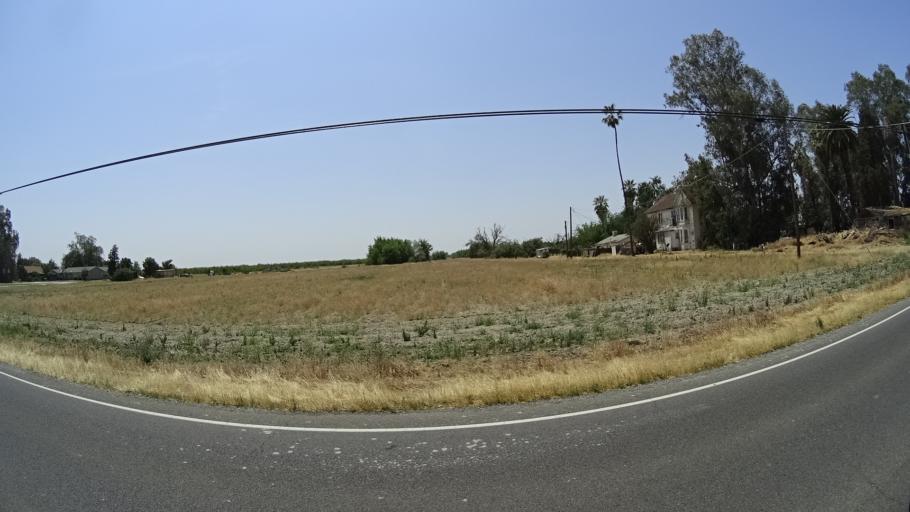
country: US
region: California
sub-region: Kings County
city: Armona
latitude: 36.3135
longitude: -119.7401
